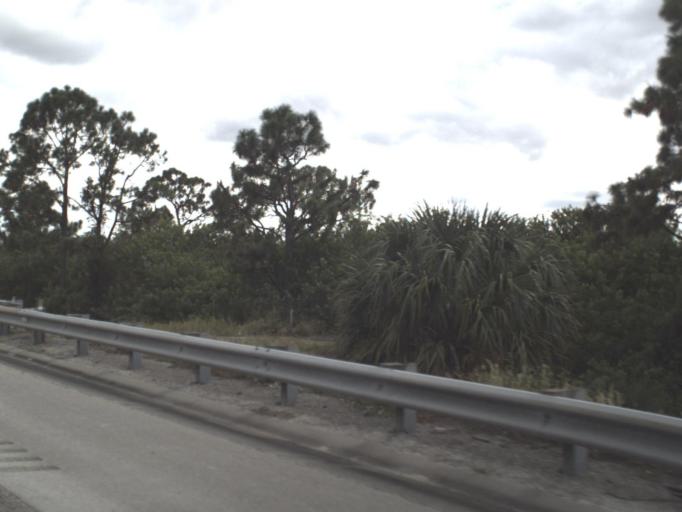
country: US
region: Florida
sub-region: Martin County
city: Hobe Sound
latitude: 27.0329
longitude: -80.2373
